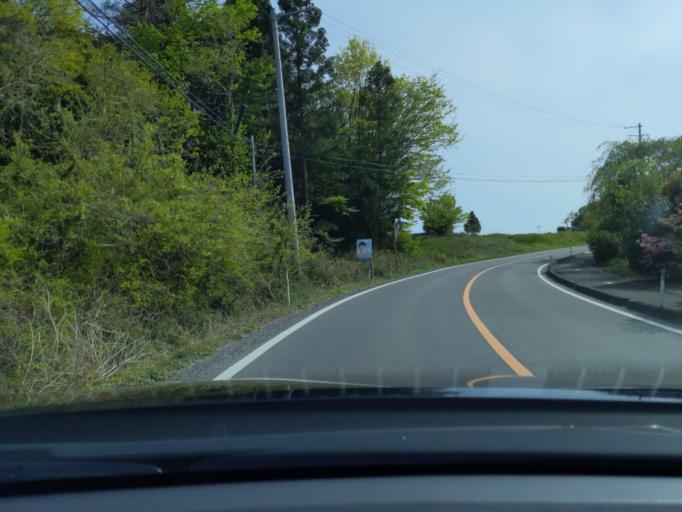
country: JP
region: Fukushima
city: Koriyama
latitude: 37.3589
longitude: 140.4185
